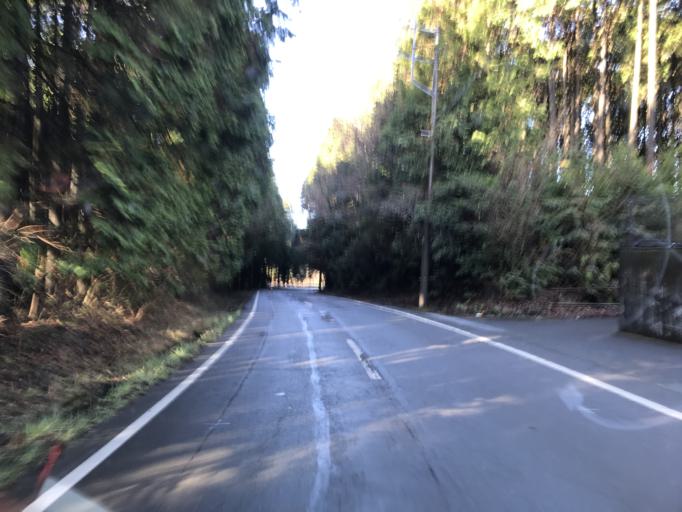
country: JP
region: Shizuoka
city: Fujinomiya
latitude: 35.2444
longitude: 138.6851
